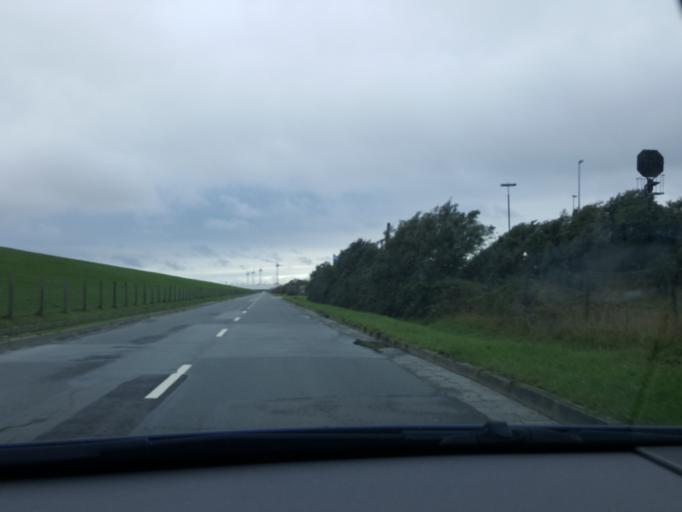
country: DE
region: Lower Saxony
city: Emden
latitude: 53.3336
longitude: 7.2113
